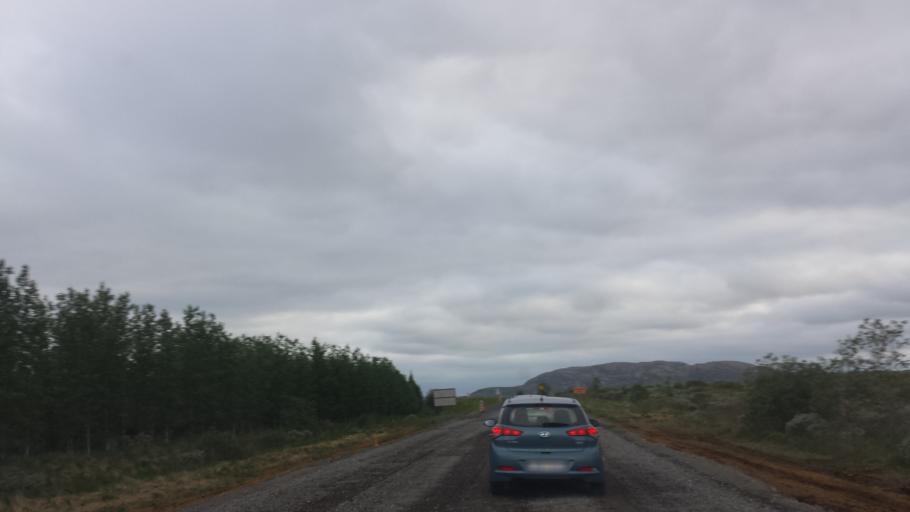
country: IS
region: South
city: Selfoss
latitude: 64.1630
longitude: -20.5280
